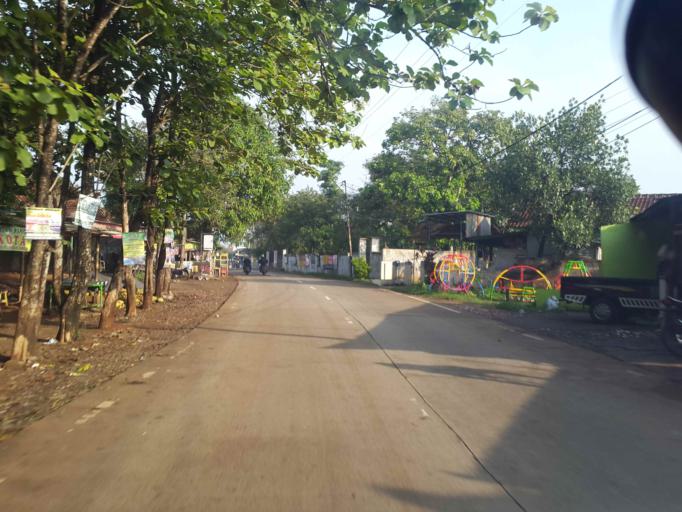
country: ID
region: West Java
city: Cileungsir
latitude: -6.3327
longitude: 107.0426
